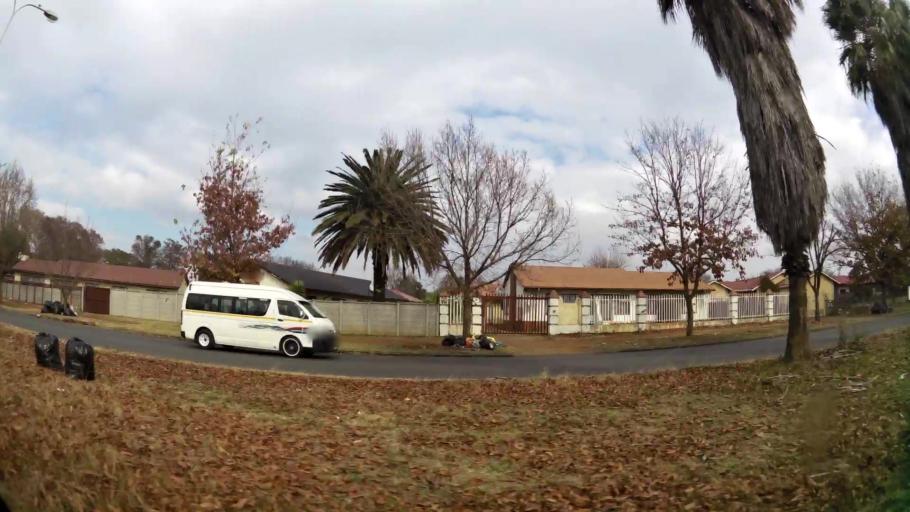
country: ZA
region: Gauteng
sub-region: Sedibeng District Municipality
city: Vanderbijlpark
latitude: -26.6974
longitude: 27.8554
